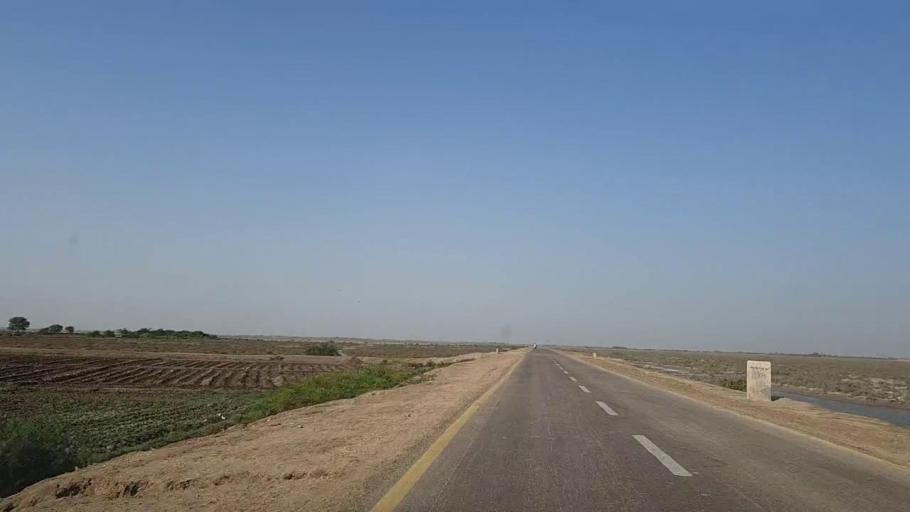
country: PK
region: Sindh
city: Jati
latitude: 24.4856
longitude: 68.3742
